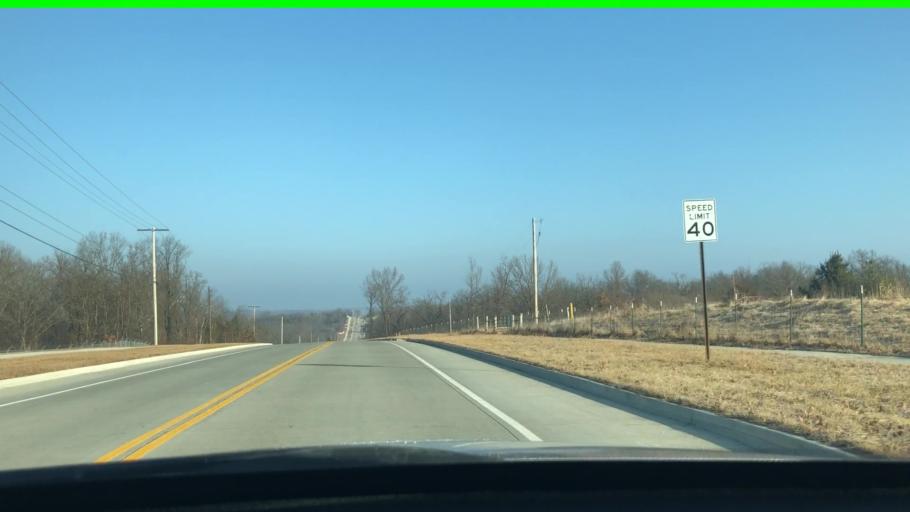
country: US
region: Missouri
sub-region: Boone County
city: Columbia
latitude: 38.8969
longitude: -92.4005
